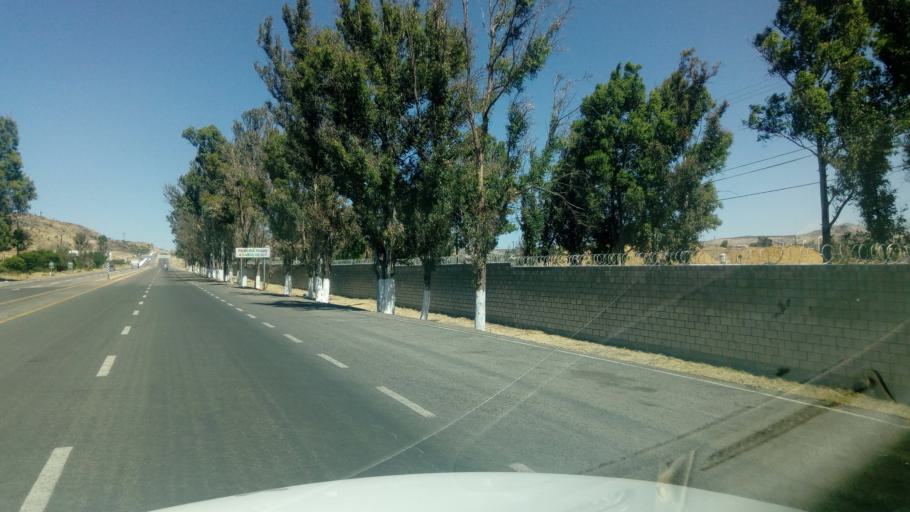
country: MX
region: Durango
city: Victoria de Durango
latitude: 24.0792
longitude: -104.6677
